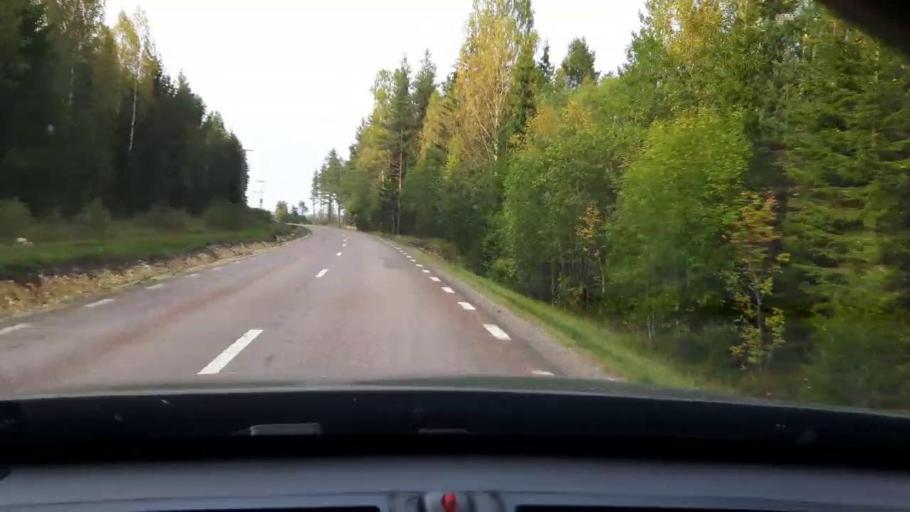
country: SE
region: Dalarna
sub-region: Gagnefs Kommun
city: Mockfjard
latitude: 60.3093
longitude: 14.9442
